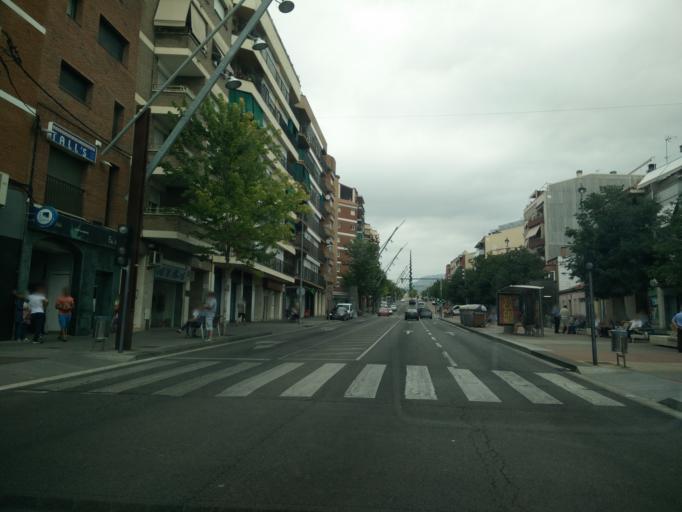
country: ES
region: Catalonia
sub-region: Provincia de Barcelona
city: Terrassa
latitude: 41.5646
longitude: 2.0271
